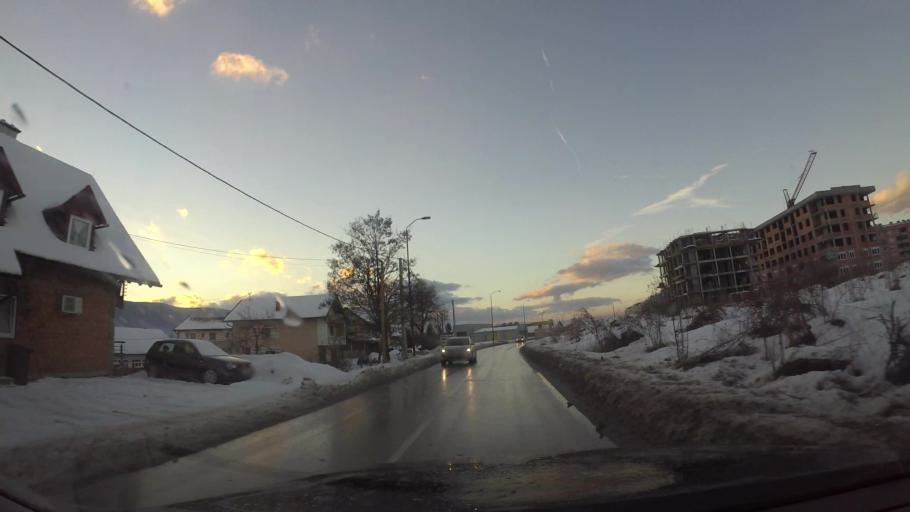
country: BA
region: Federation of Bosnia and Herzegovina
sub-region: Kanton Sarajevo
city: Sarajevo
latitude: 43.8154
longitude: 18.3627
